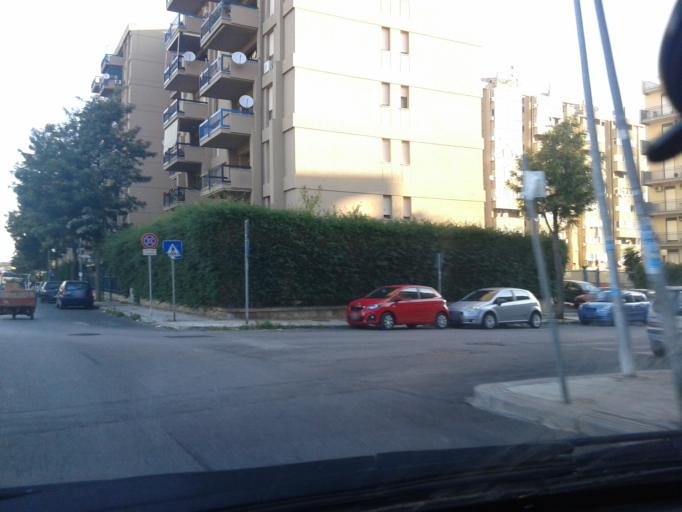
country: IT
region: Sicily
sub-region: Palermo
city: Ciaculli
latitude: 38.0848
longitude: 13.3620
